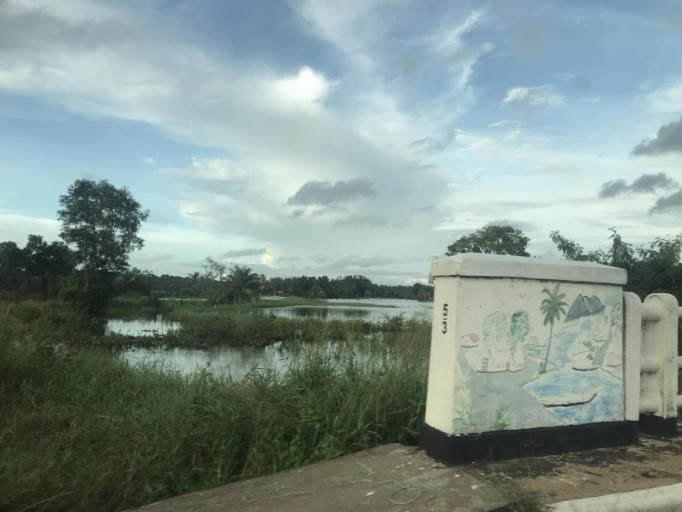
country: LK
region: Western
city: Ja Ela
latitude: 7.1051
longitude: 79.9240
